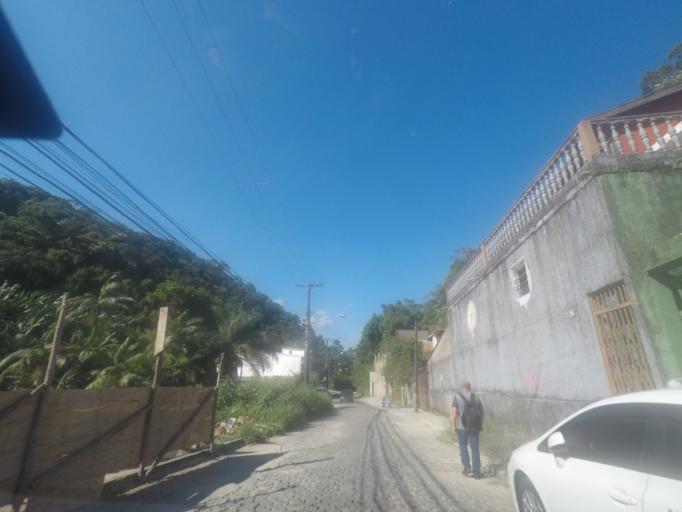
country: BR
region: Rio de Janeiro
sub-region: Petropolis
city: Petropolis
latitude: -22.5410
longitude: -43.2022
